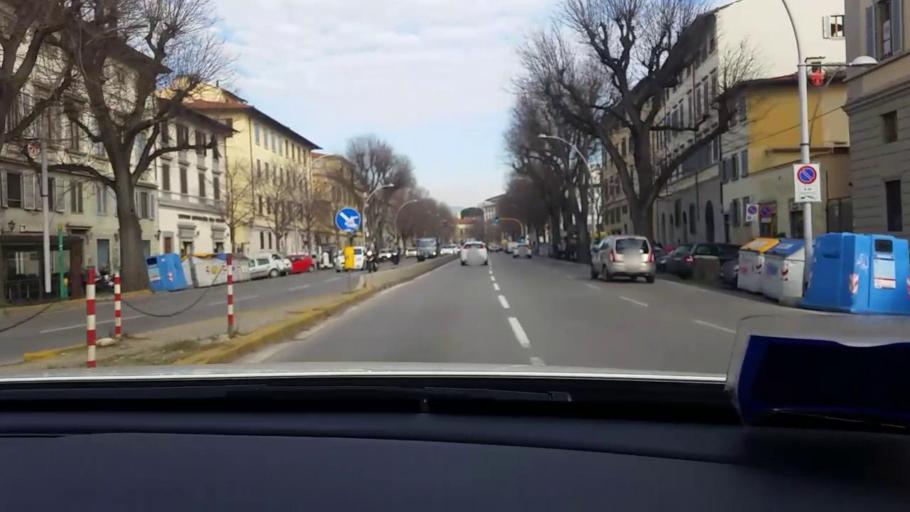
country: IT
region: Tuscany
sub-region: Province of Florence
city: Florence
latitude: 43.7710
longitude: 11.2710
